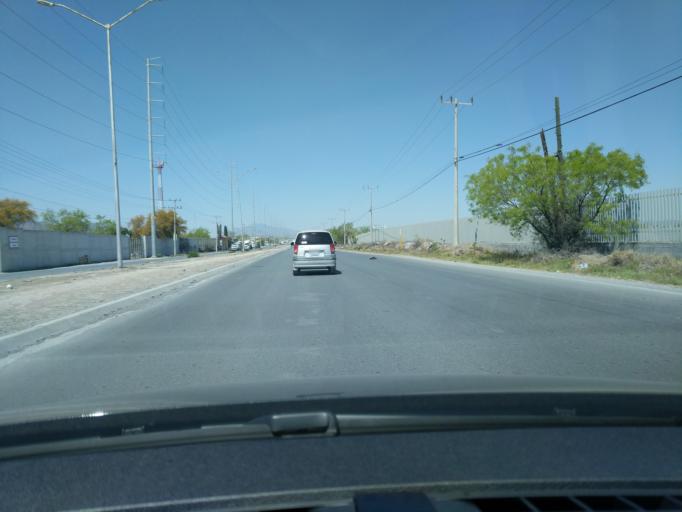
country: MX
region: Nuevo Leon
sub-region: Salinas Victoria
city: Emiliano Zapata
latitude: 25.9014
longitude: -100.2630
